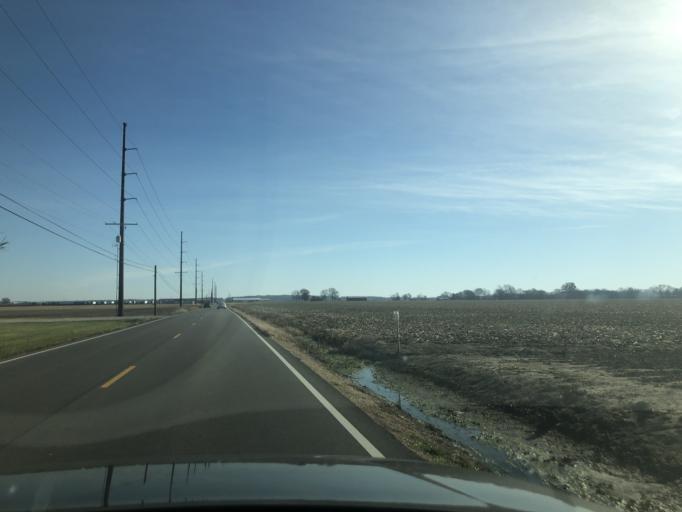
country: US
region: Indiana
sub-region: Warrick County
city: Newburgh
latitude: 37.9912
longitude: -87.4554
